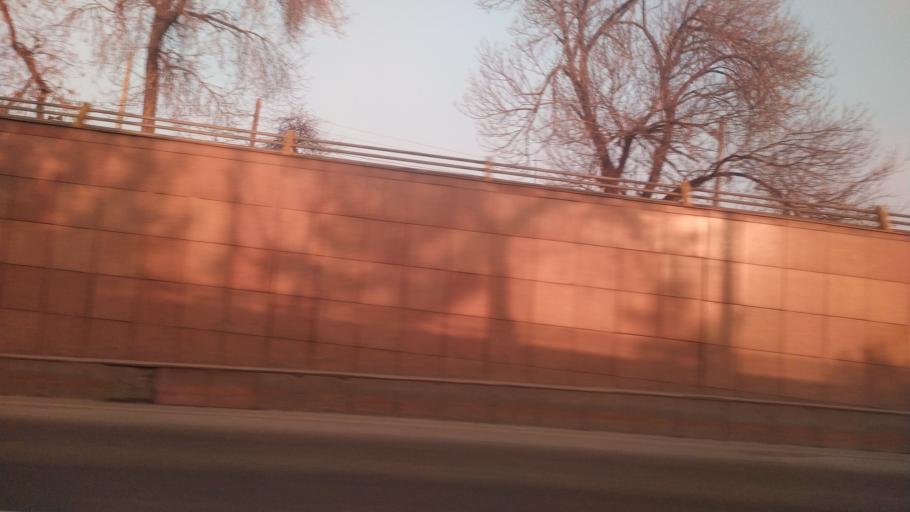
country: KZ
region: Almaty Qalasy
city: Almaty
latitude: 43.2597
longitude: 76.8883
